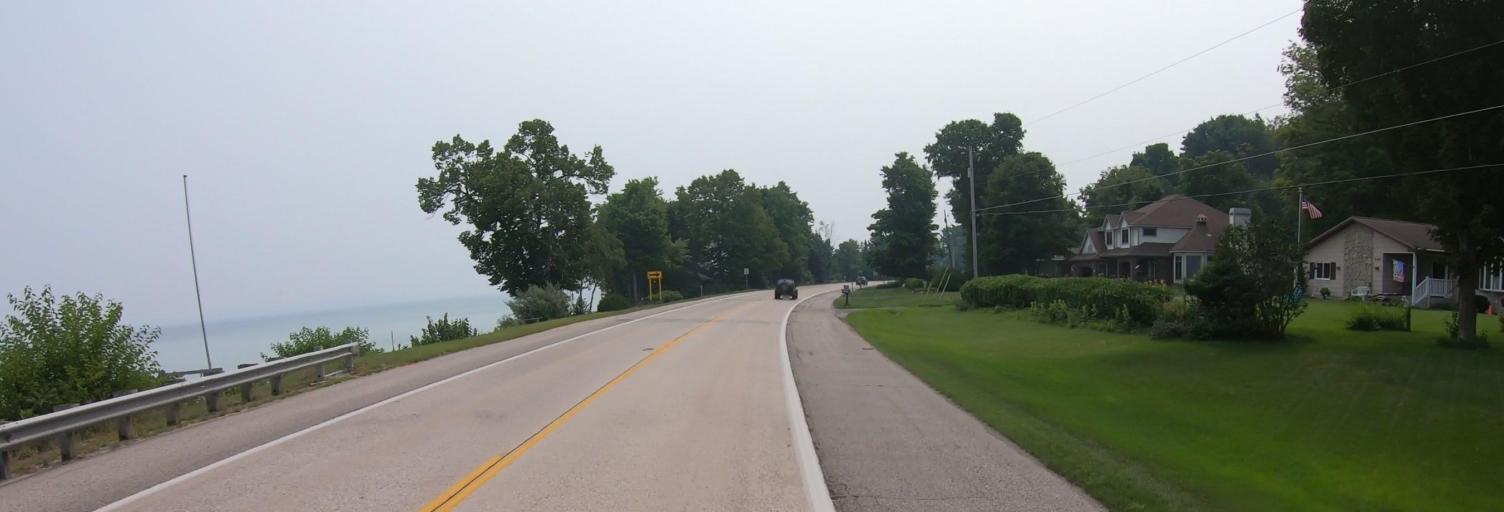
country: US
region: Michigan
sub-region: Leelanau County
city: Greilickville
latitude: 44.8623
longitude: -85.6492
